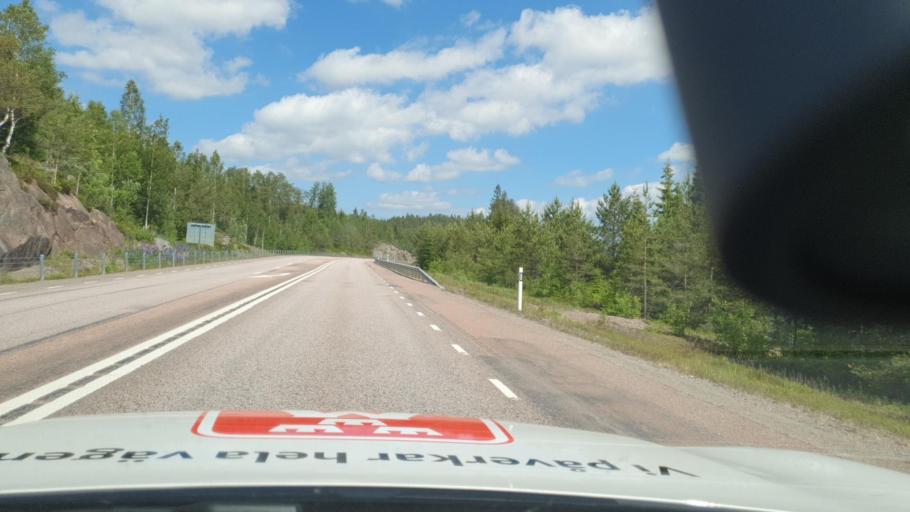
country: SE
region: Vaermland
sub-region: Filipstads Kommun
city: Filipstad
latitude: 59.6922
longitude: 14.0854
